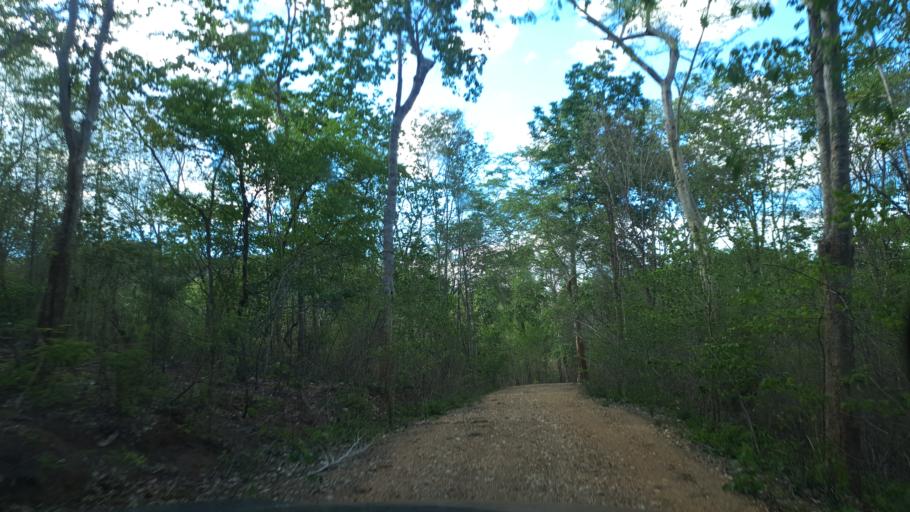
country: TH
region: Lampang
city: Sop Prap
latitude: 17.8456
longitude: 99.2857
